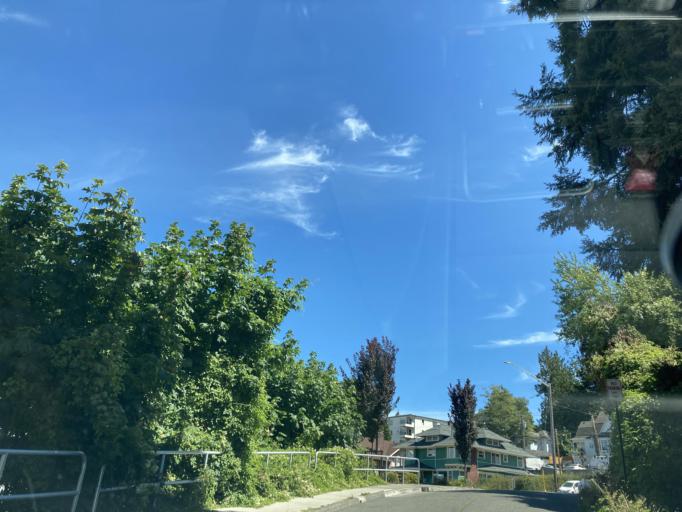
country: US
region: Washington
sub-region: Whatcom County
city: Bellingham
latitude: 48.7430
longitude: -122.4819
